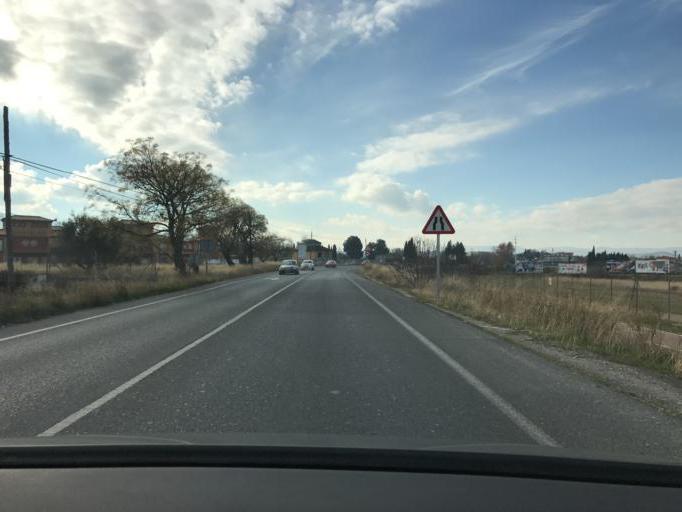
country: ES
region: Andalusia
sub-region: Provincia de Granada
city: Alhendin
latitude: 37.1193
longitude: -3.6320
